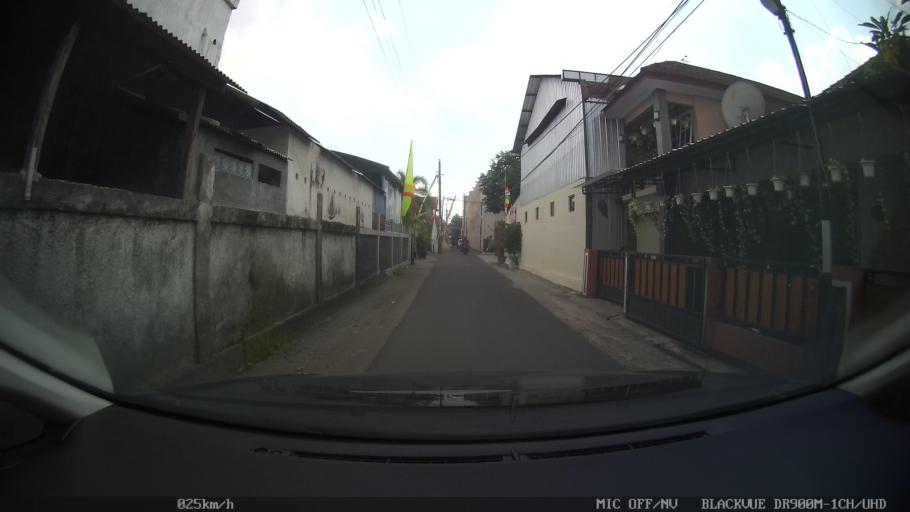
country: ID
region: Daerah Istimewa Yogyakarta
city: Yogyakarta
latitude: -7.8056
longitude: 110.4039
